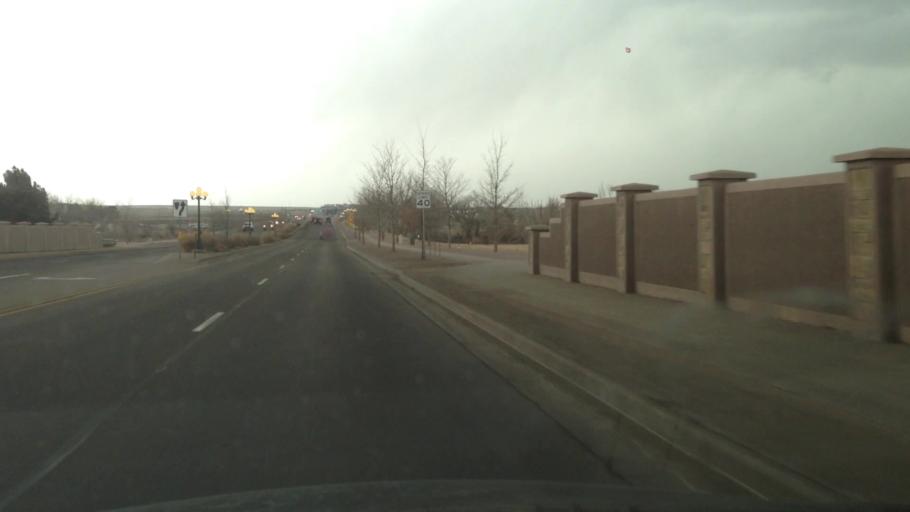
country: US
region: Colorado
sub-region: Douglas County
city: Parker
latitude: 39.4931
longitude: -104.7650
